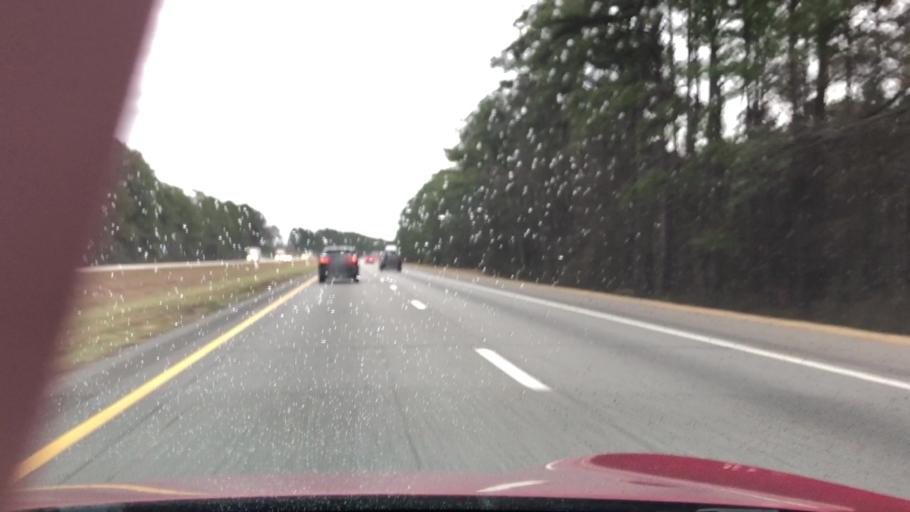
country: US
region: South Carolina
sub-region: Dillon County
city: Latta
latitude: 34.3685
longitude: -79.4937
